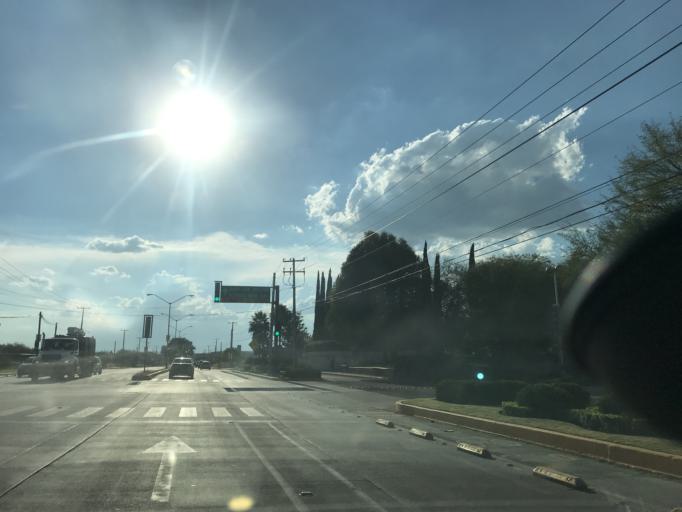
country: MX
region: Aguascalientes
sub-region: Aguascalientes
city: Pocitos
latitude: 21.9098
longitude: -102.3248
